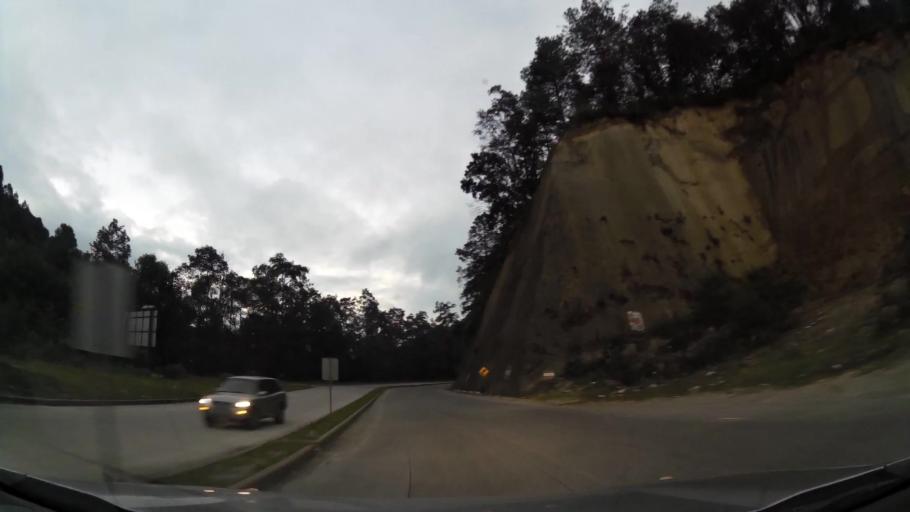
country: GT
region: Chimaltenango
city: Santa Apolonia
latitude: 14.8445
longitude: -91.0486
